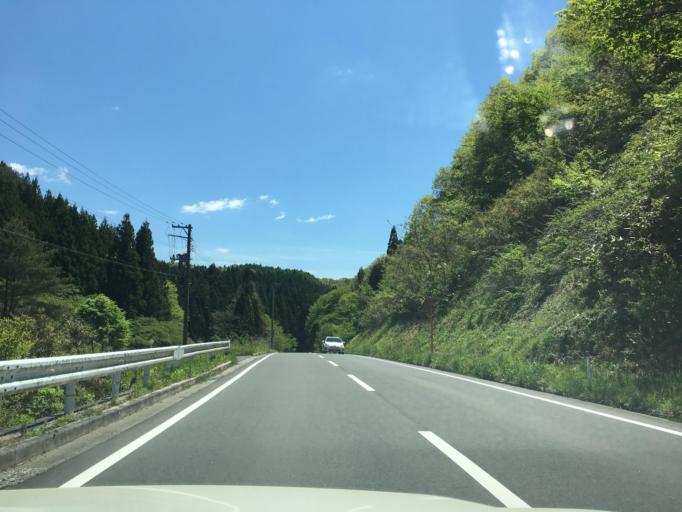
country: JP
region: Fukushima
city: Funehikimachi-funehiki
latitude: 37.3348
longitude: 140.6257
